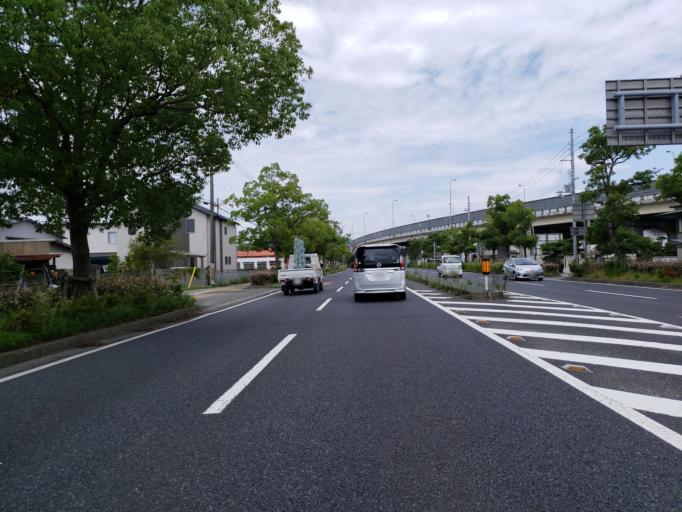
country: JP
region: Hyogo
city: Kakogawacho-honmachi
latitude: 34.7849
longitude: 134.7819
